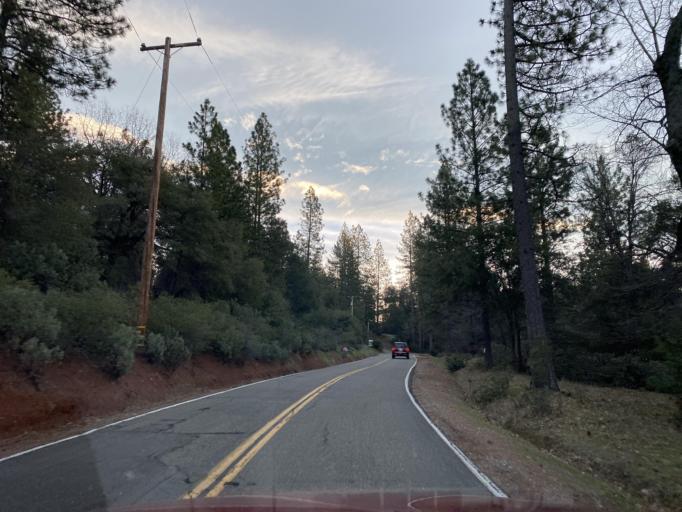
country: US
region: California
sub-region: Amador County
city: Pine Grove
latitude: 38.5015
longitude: -120.6538
